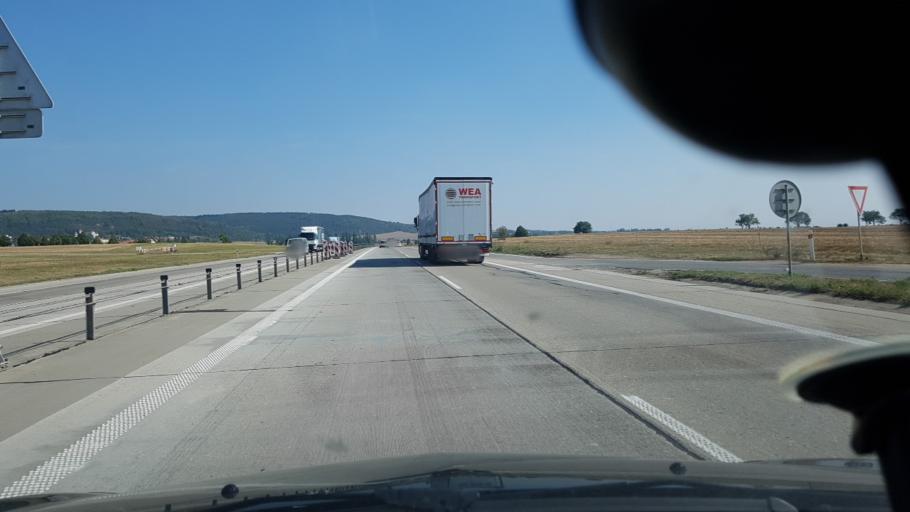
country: CZ
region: South Moravian
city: Pustimer
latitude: 49.3074
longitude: 17.0312
